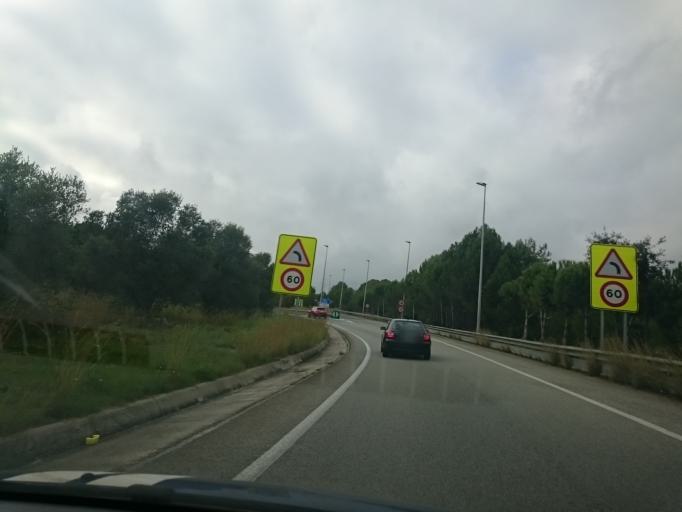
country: ES
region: Catalonia
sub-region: Provincia de Barcelona
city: Sant Pere de Ribes
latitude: 41.2435
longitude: 1.7615
